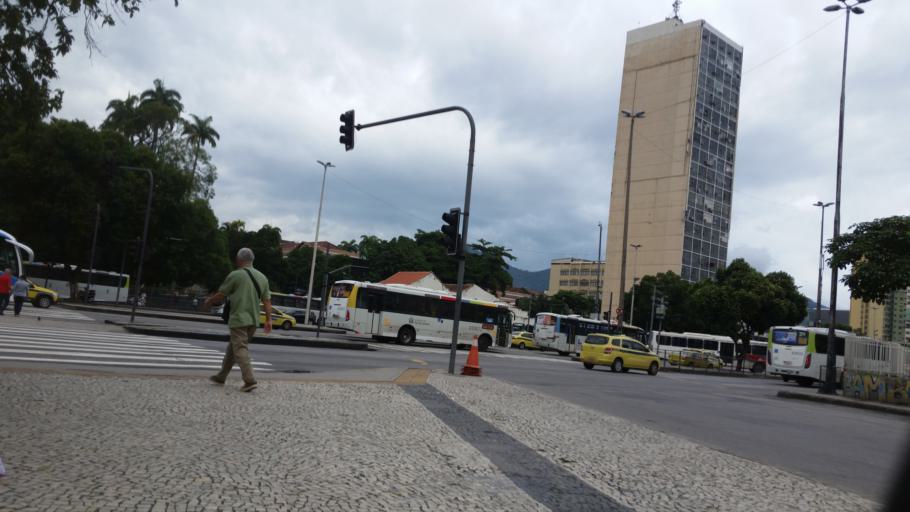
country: BR
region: Rio de Janeiro
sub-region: Rio De Janeiro
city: Rio de Janeiro
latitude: -22.9045
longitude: -43.1905
